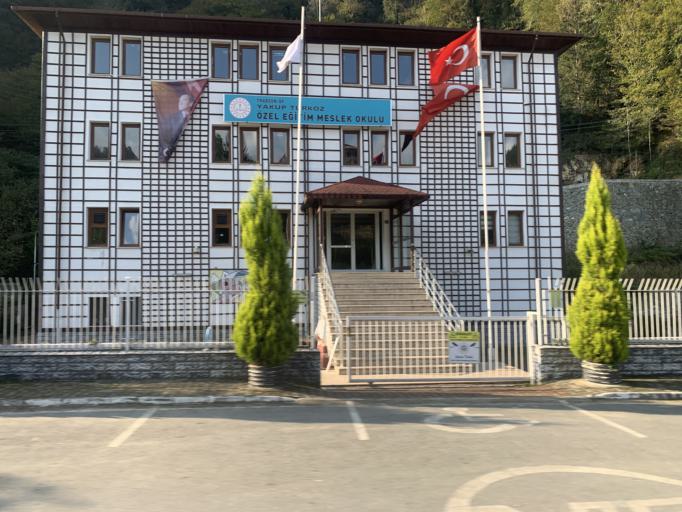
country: TR
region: Trabzon
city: Dernekpazari
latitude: 40.8341
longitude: 40.2707
